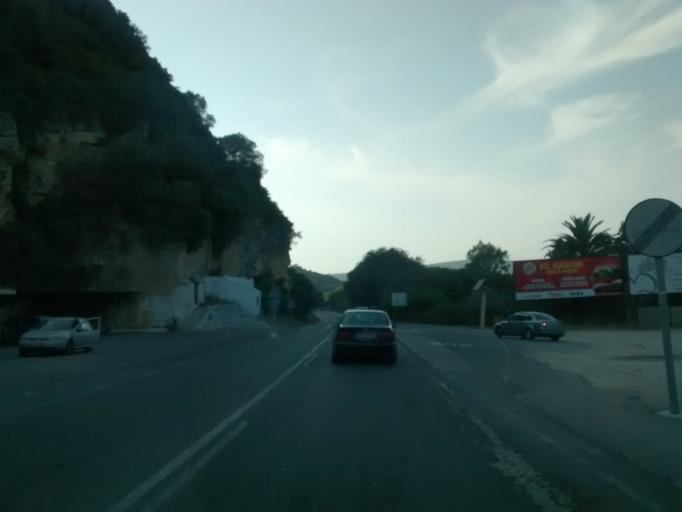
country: ES
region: Andalusia
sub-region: Provincia de Cadiz
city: Vejer de la Frontera
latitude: 36.2537
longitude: -5.9569
